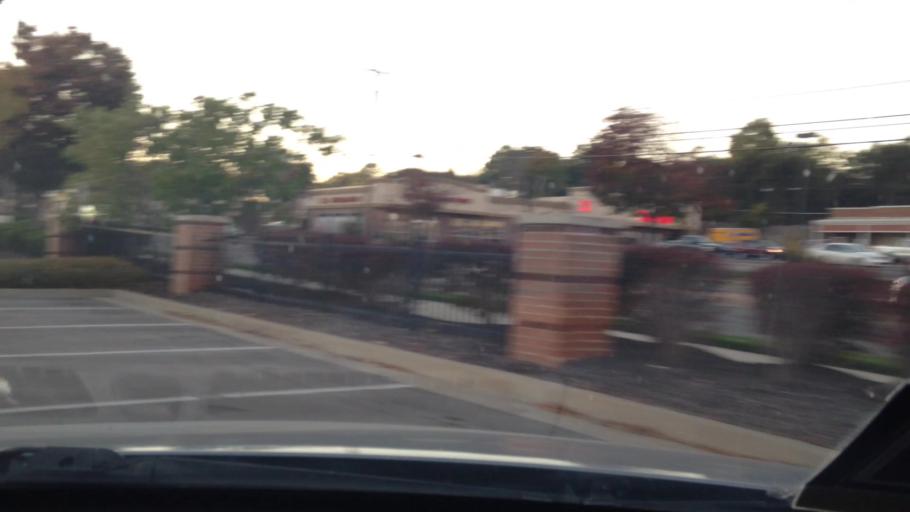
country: US
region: Kansas
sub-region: Johnson County
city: Overland Park
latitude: 38.9565
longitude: -94.6876
